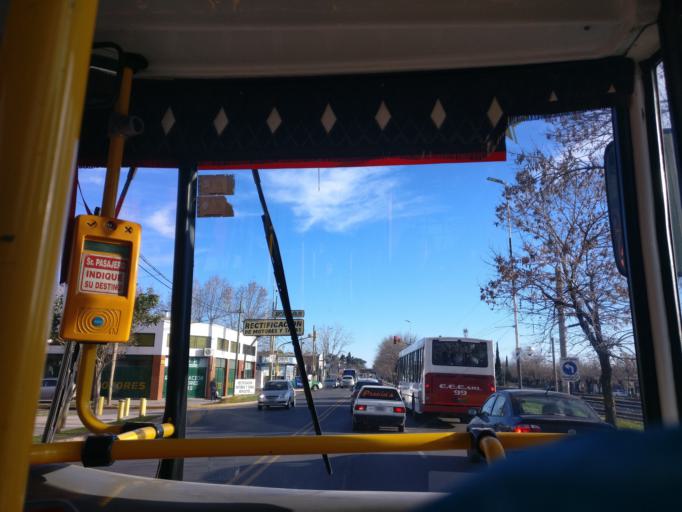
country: AR
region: Buenos Aires
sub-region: Partido de Ezeiza
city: Ezeiza
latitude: -34.8580
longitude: -58.5274
